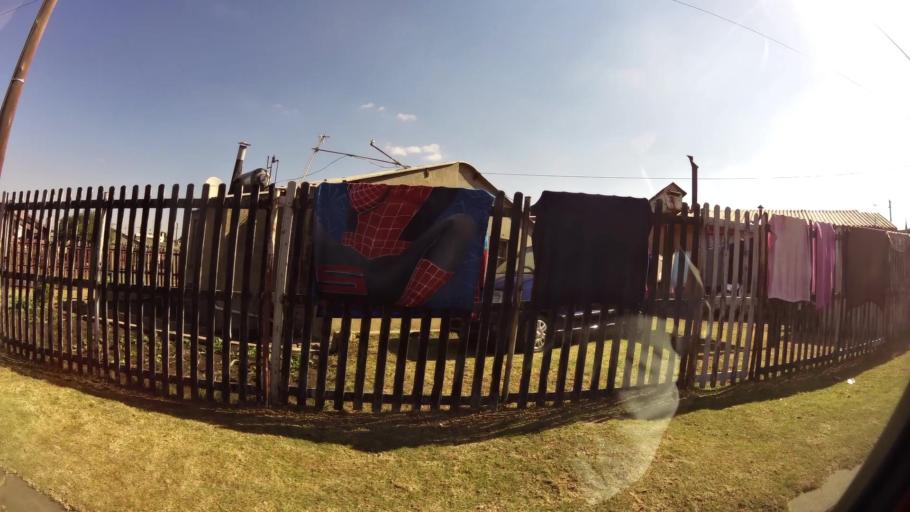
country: ZA
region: Gauteng
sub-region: City of Johannesburg Metropolitan Municipality
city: Soweto
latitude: -26.2432
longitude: 27.9001
